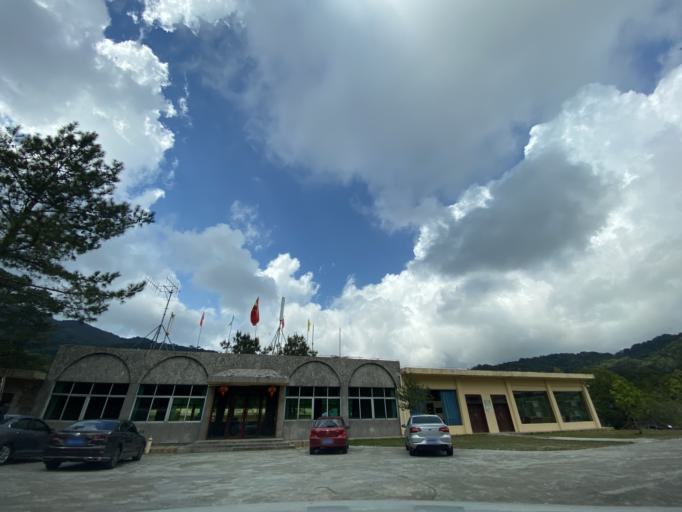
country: CN
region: Hainan
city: Diaoluoshan
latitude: 18.7253
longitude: 109.8684
